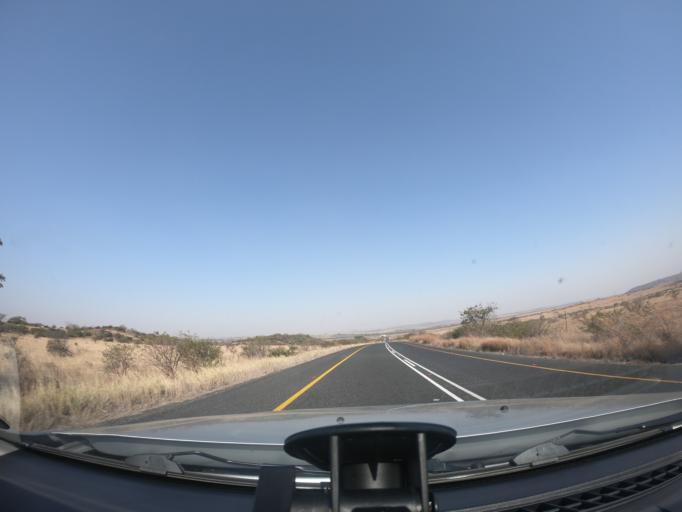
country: ZA
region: KwaZulu-Natal
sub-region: uThukela District Municipality
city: Ladysmith
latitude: -28.7172
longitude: 29.8155
